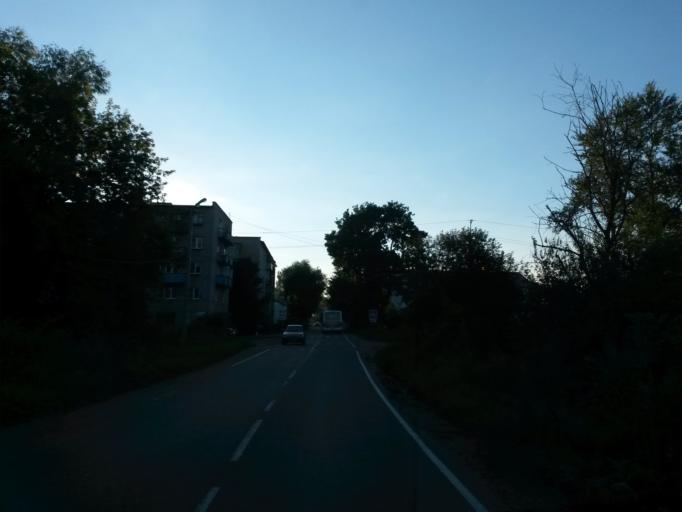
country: RU
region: Jaroslavl
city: Tutayev
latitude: 57.8746
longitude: 39.5211
